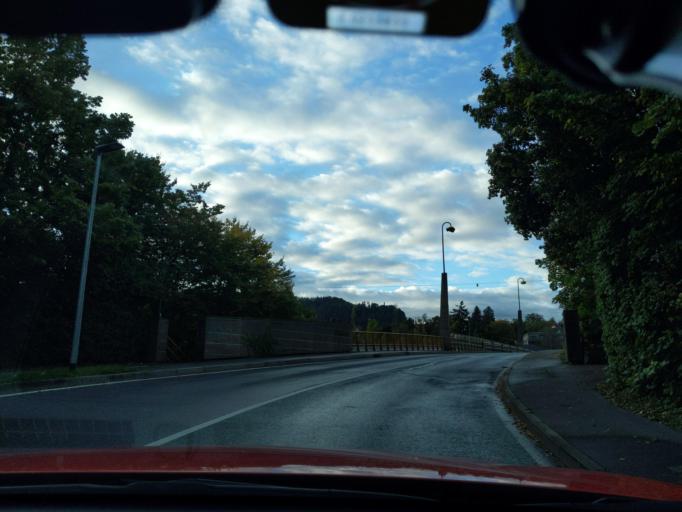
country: AT
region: Vorarlberg
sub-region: Politischer Bezirk Bregenz
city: Bregenz
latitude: 47.5029
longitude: 9.7367
